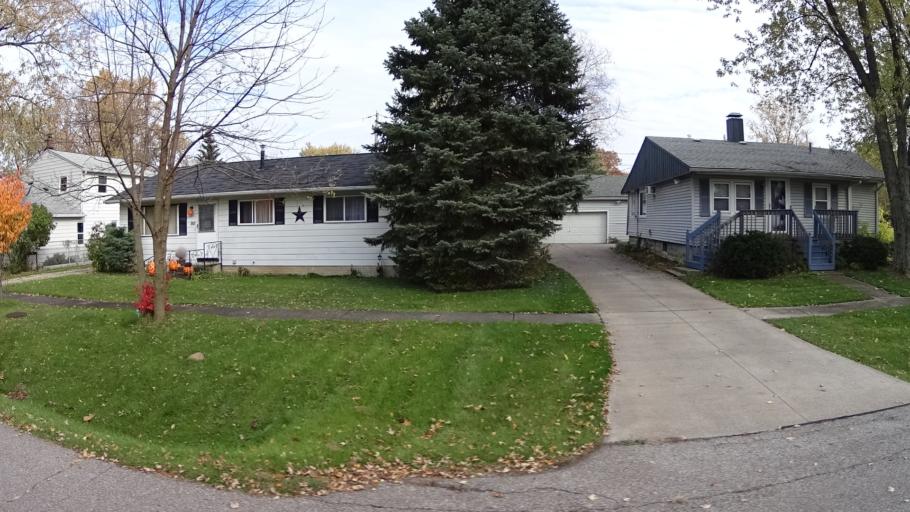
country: US
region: Ohio
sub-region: Lorain County
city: Sheffield Lake
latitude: 41.4910
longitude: -82.0974
